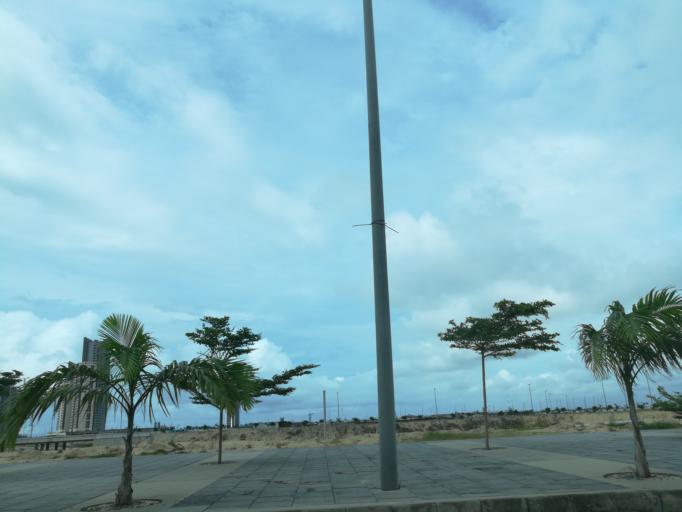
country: NG
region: Lagos
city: Ikoyi
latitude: 6.4143
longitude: 3.4157
